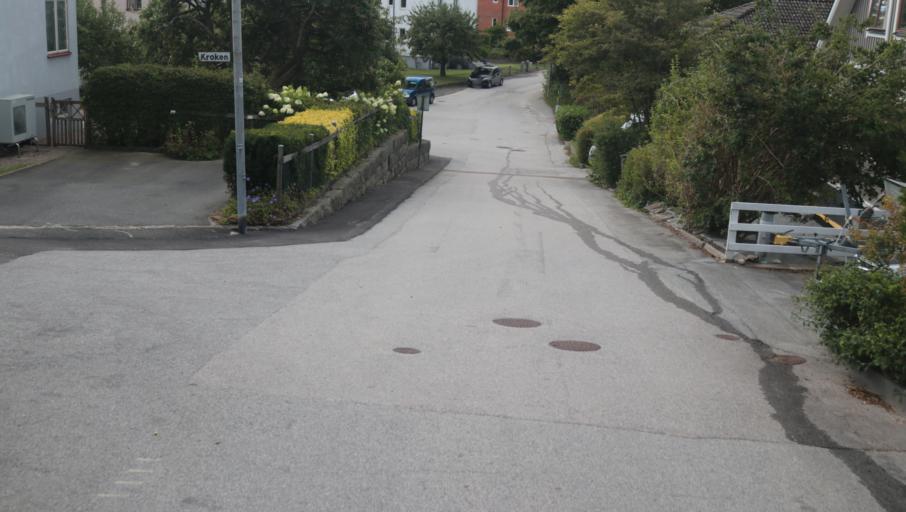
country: SE
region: Blekinge
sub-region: Karlshamns Kommun
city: Karlshamn
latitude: 56.1711
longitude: 14.8732
